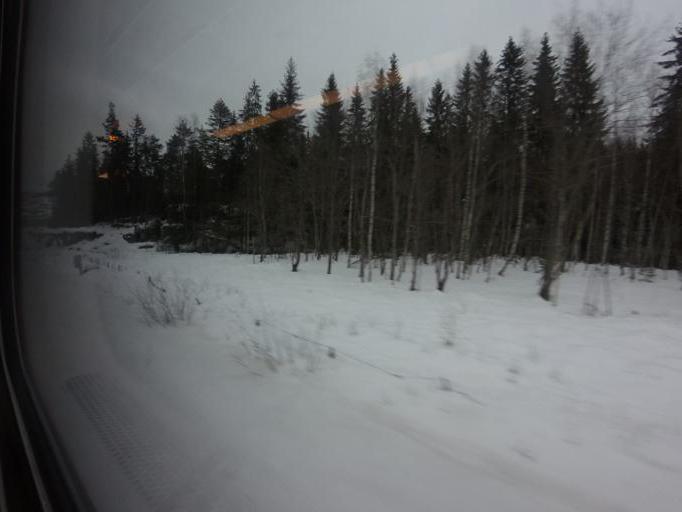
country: NO
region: Oppland
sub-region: Lillehammer
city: Lillehammer
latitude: 61.2052
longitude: 10.4241
